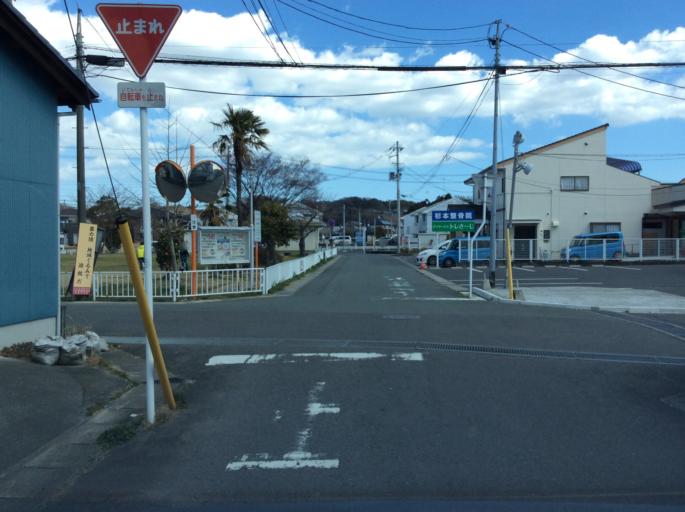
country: JP
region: Fukushima
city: Iwaki
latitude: 36.9568
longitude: 140.9048
